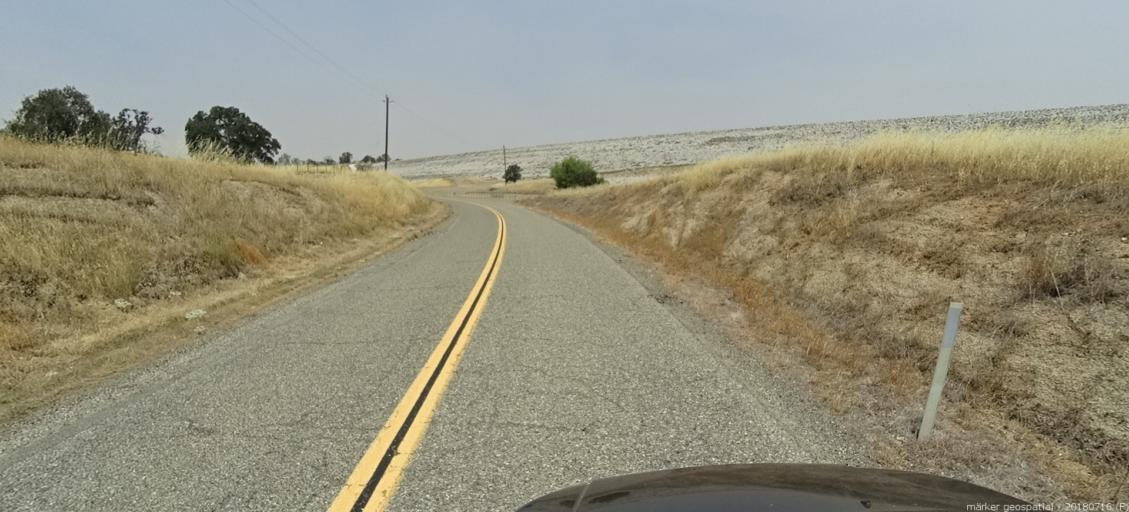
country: US
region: California
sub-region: Madera County
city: Bonadelle Ranchos-Madera Ranchos
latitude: 37.1110
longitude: -119.8893
